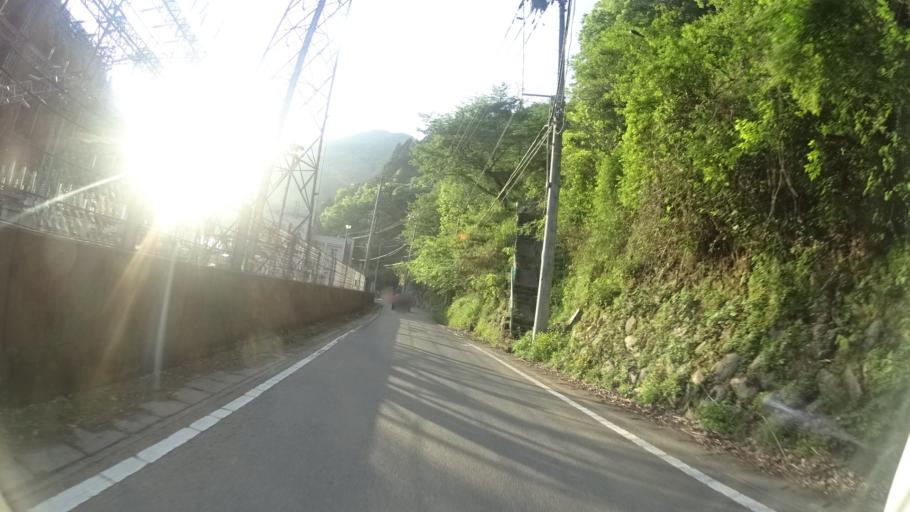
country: JP
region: Tokushima
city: Ikedacho
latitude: 33.9555
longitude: 133.8024
